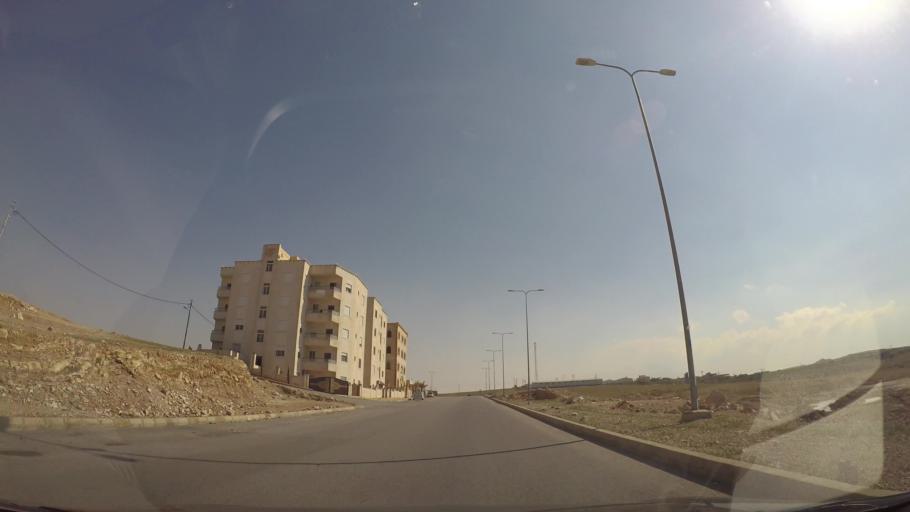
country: JO
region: Zarqa
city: Zarqa
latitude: 32.0484
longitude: 36.1165
